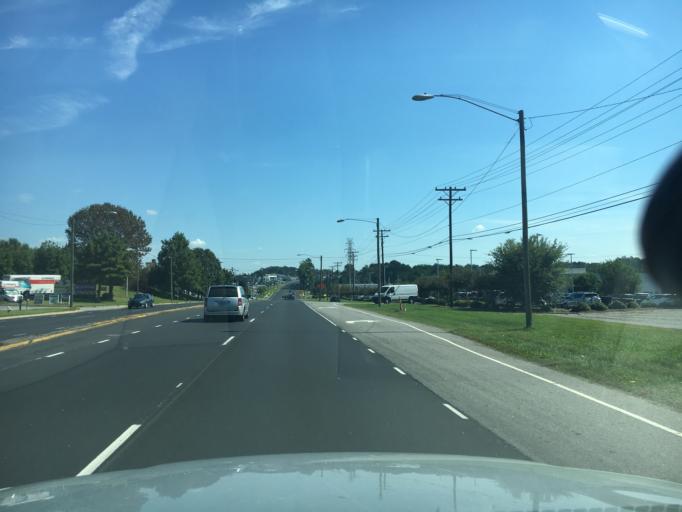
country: US
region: North Carolina
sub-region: Catawba County
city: Hickory
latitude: 35.7112
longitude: -81.3230
